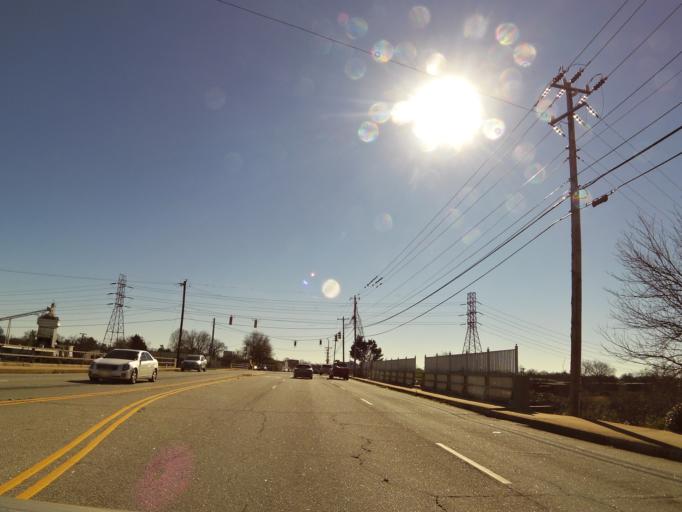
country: US
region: South Carolina
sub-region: Greenville County
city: Sans Souci
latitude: 34.8789
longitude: -82.4046
